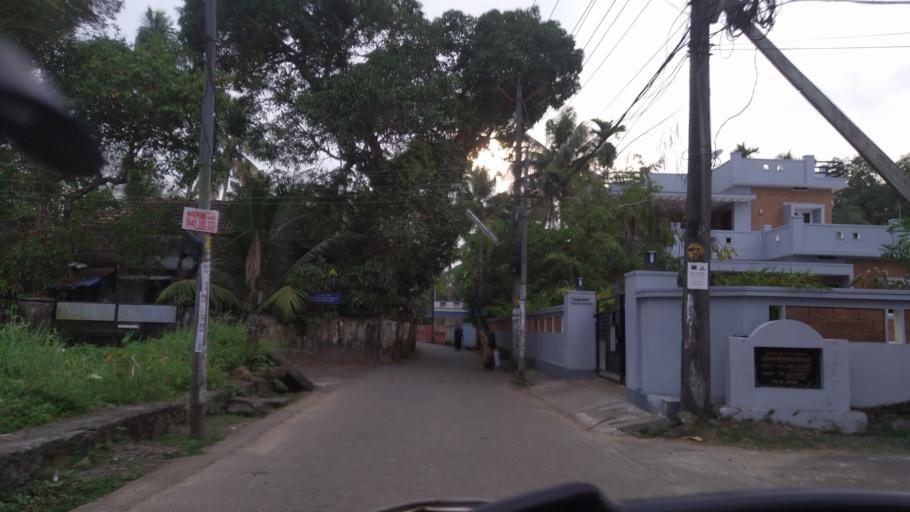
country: IN
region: Kerala
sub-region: Thrissur District
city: Kodungallur
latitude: 10.1384
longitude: 76.2231
